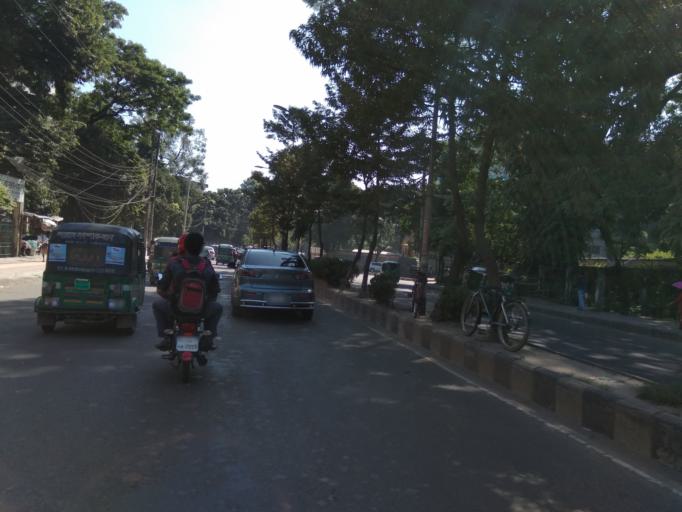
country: BD
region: Dhaka
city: Paltan
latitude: 23.7447
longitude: 90.4046
